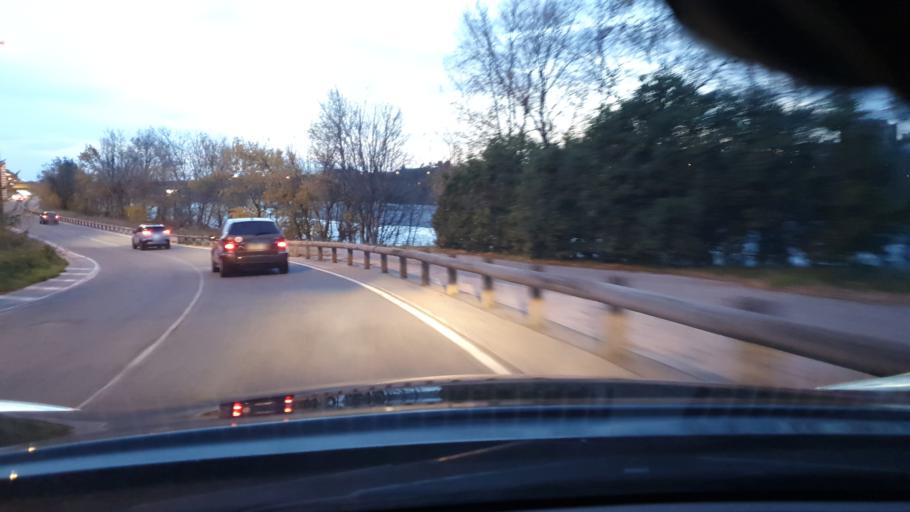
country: FR
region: Provence-Alpes-Cote d'Azur
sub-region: Departement des Alpes-Maritimes
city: Saint-Laurent-du-Var
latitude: 43.6732
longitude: 7.1966
